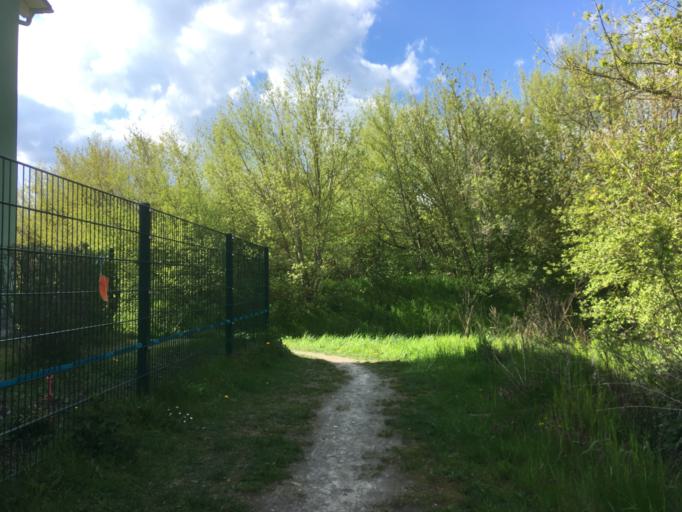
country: DE
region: Berlin
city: Hellersdorf
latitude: 52.5375
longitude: 13.6284
